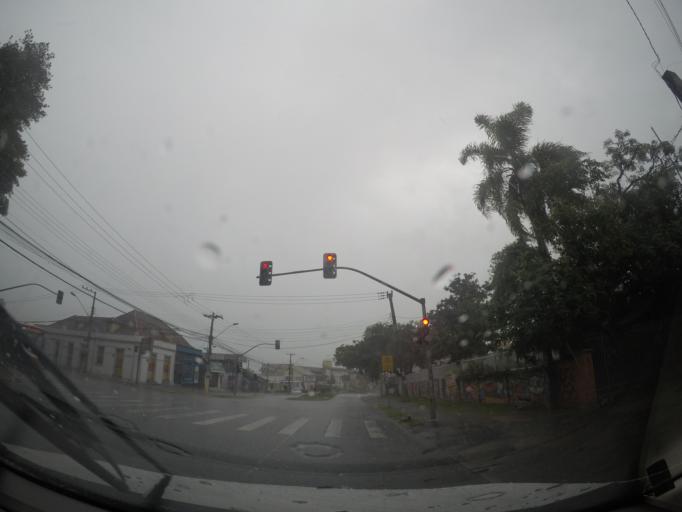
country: BR
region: Parana
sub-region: Curitiba
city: Curitiba
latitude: -25.4493
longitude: -49.3518
